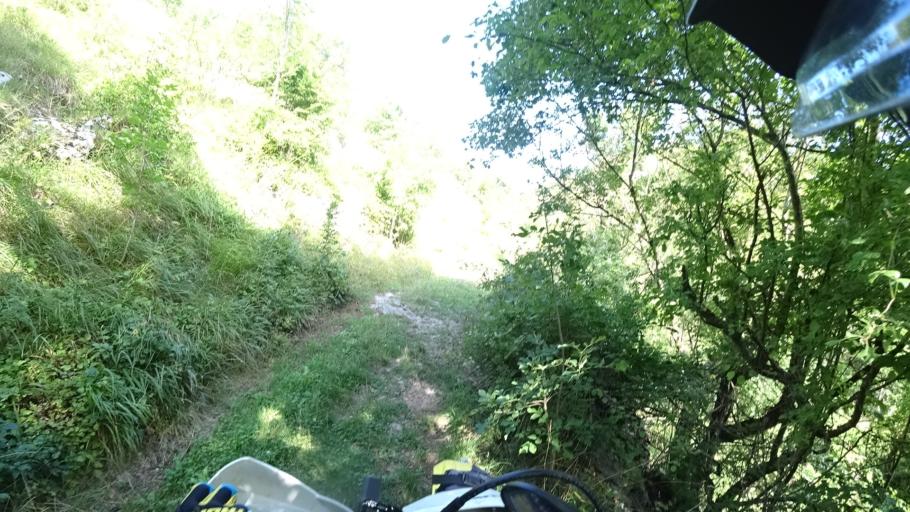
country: HR
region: Zadarska
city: Gracac
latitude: 44.3258
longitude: 15.9711
